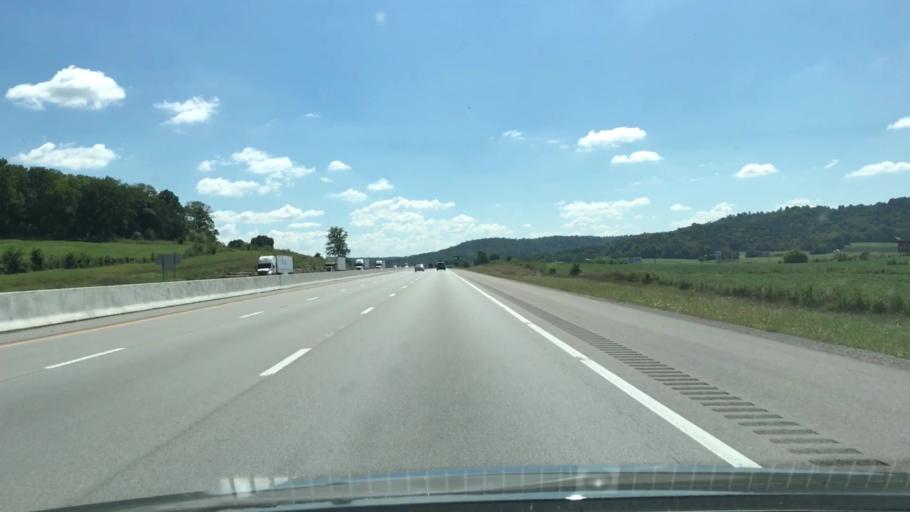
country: US
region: Kentucky
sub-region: Hart County
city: Horse Cave
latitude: 37.2213
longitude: -85.9345
